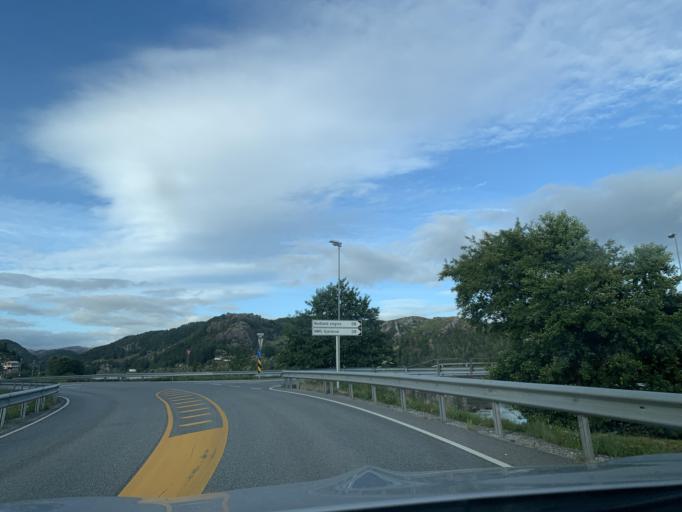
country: NO
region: Rogaland
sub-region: Eigersund
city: Egersund
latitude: 58.4606
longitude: 6.0151
